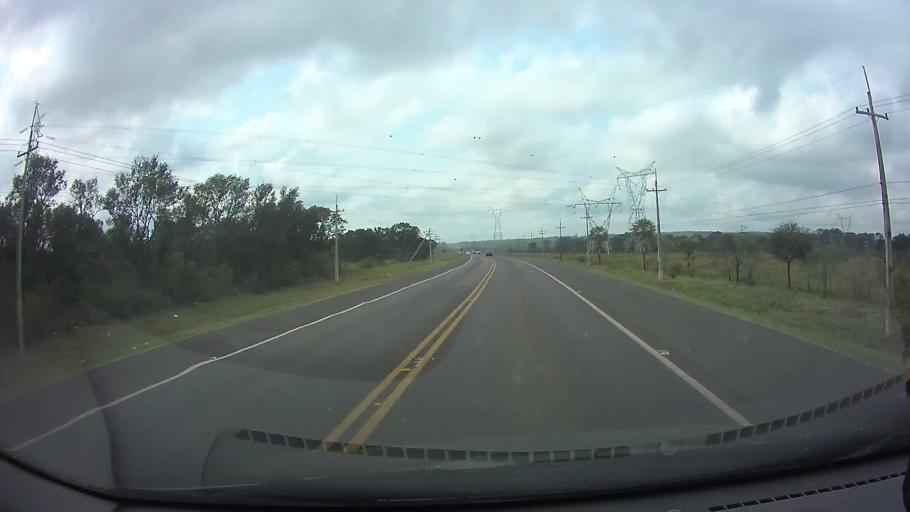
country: PY
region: Central
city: Limpio
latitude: -25.1146
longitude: -57.4240
